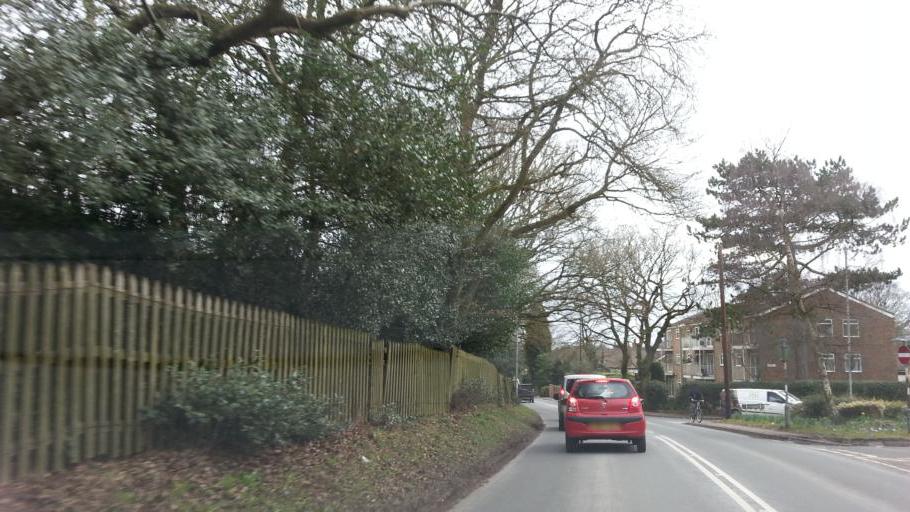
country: GB
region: England
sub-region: Walsall
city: Streetly
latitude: 52.5810
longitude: -1.8756
